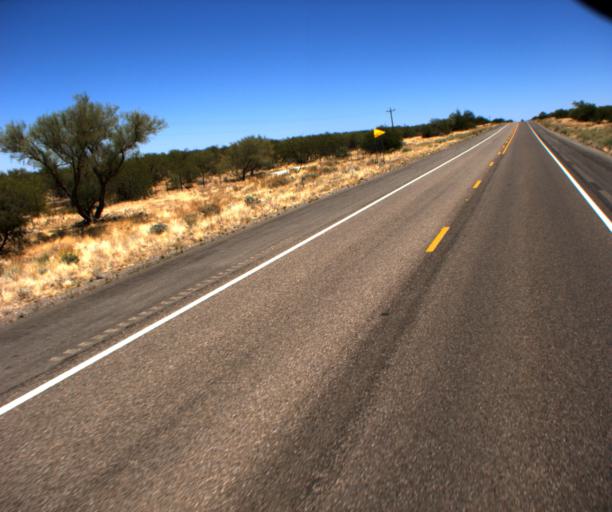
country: US
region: Arizona
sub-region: Pima County
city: Sells
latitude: 32.0184
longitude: -111.6206
